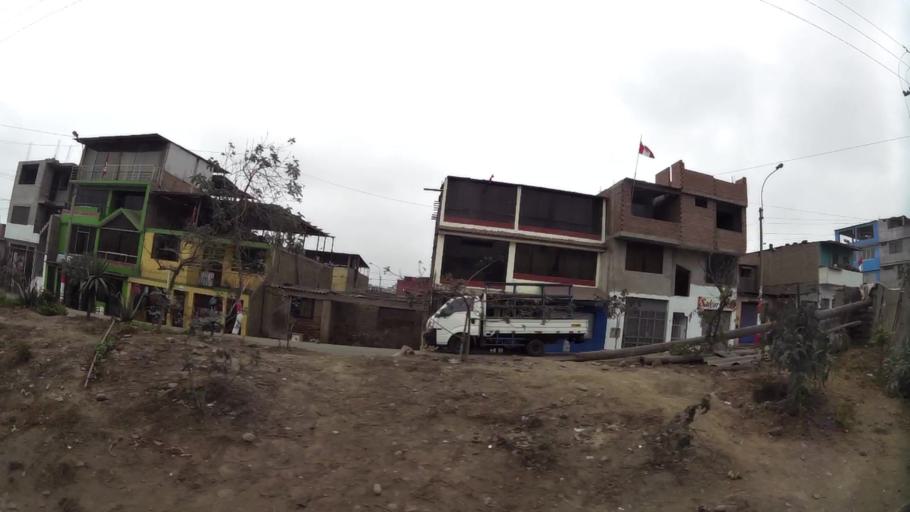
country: PE
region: Lima
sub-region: Lima
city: Surco
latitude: -12.1369
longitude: -76.9601
